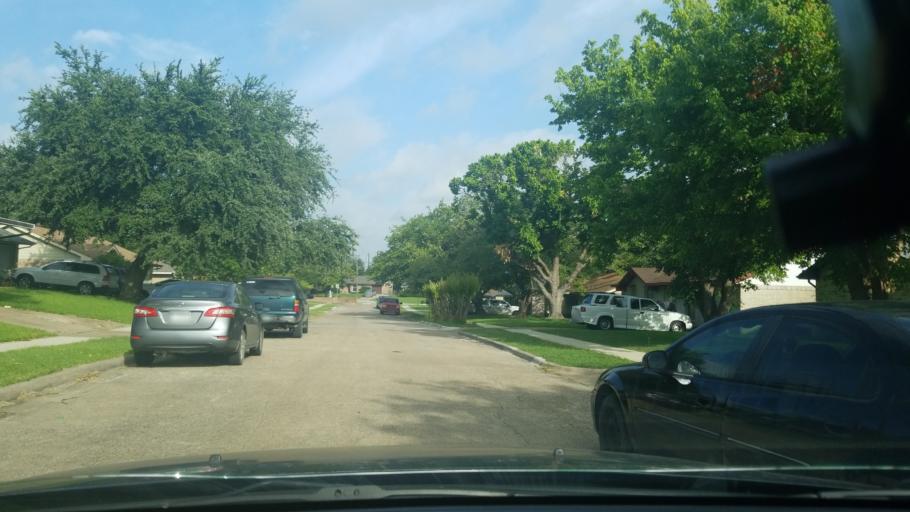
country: US
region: Texas
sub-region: Dallas County
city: Mesquite
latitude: 32.7735
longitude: -96.6417
